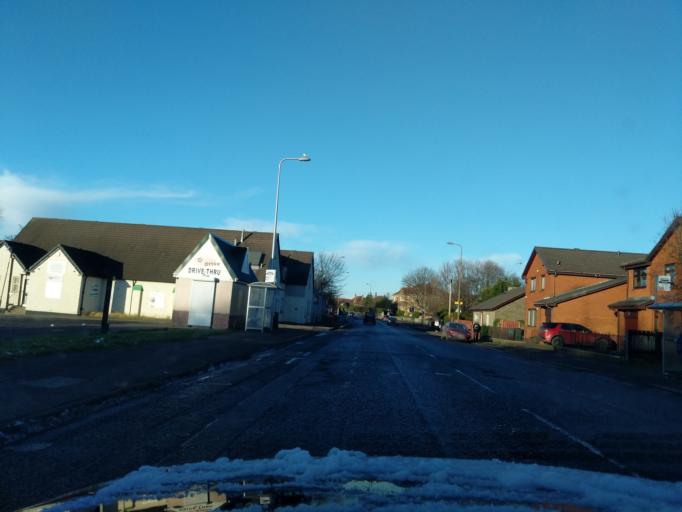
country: GB
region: Scotland
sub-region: West Lothian
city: Seafield
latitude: 55.9389
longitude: -3.1151
